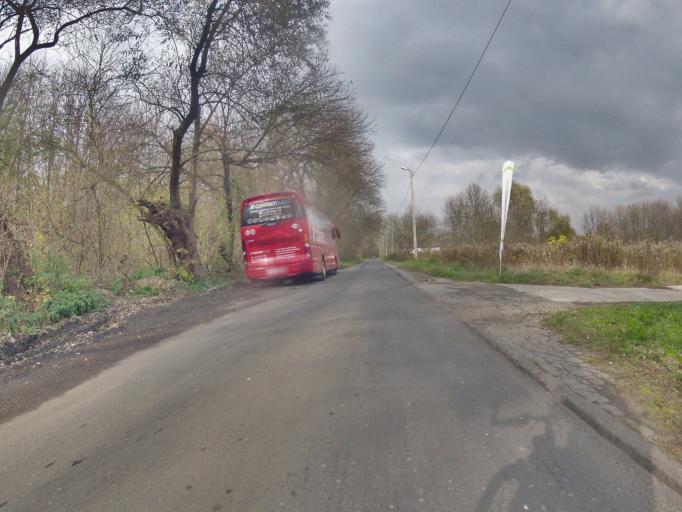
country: PL
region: Lesser Poland Voivodeship
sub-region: Powiat wielicki
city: Wegrzce Wielkie
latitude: 50.0551
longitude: 20.1018
